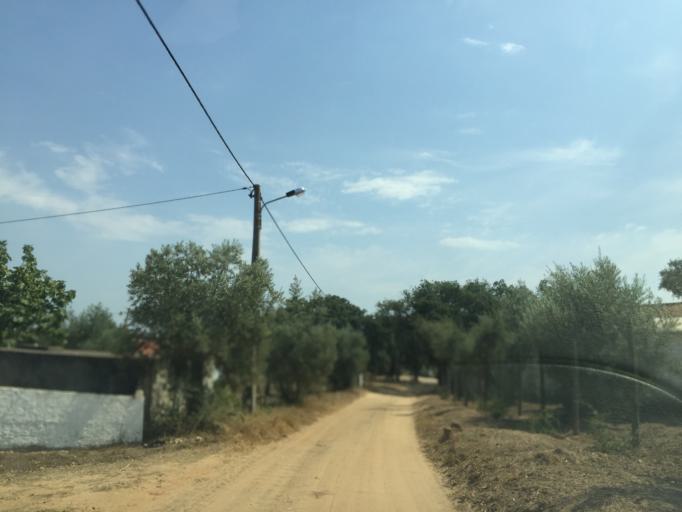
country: PT
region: Setubal
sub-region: Grandola
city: Grandola
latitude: 38.0245
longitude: -8.4840
